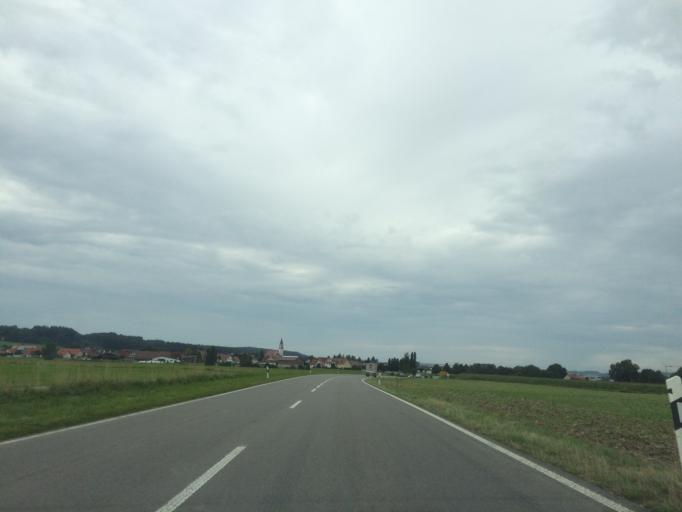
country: DE
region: Baden-Wuerttemberg
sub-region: Tuebingen Region
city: Eberhardzell
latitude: 47.9812
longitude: 9.7857
